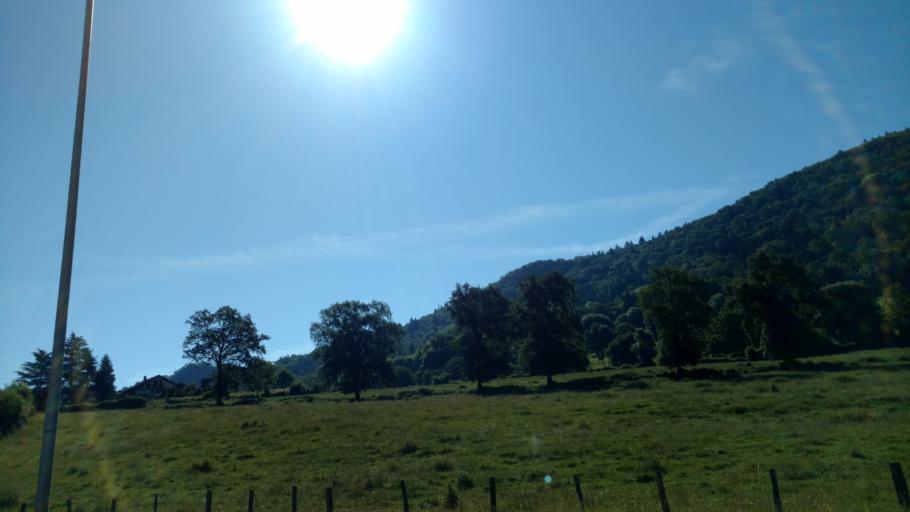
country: FR
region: Rhone-Alpes
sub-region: Departement de la Haute-Savoie
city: Margencel
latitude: 46.3288
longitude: 6.4463
